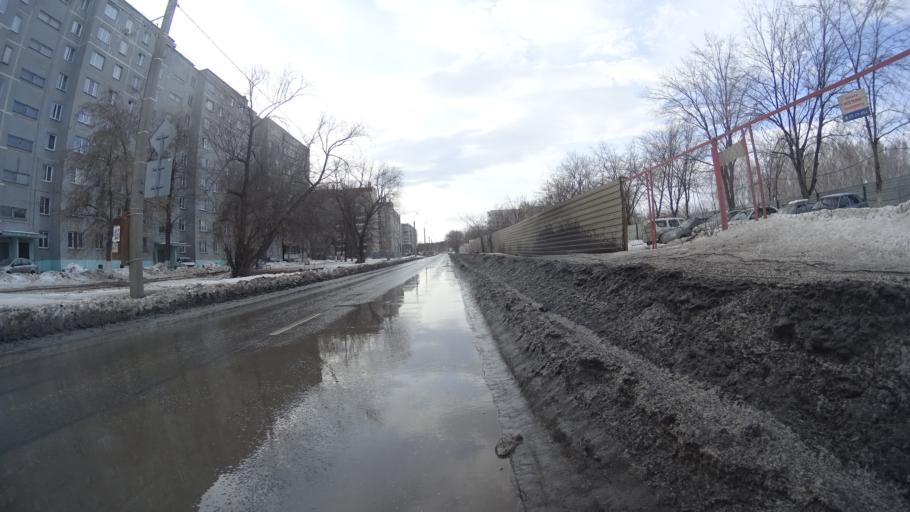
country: RU
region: Chelyabinsk
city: Roshchino
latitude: 55.1987
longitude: 61.3120
